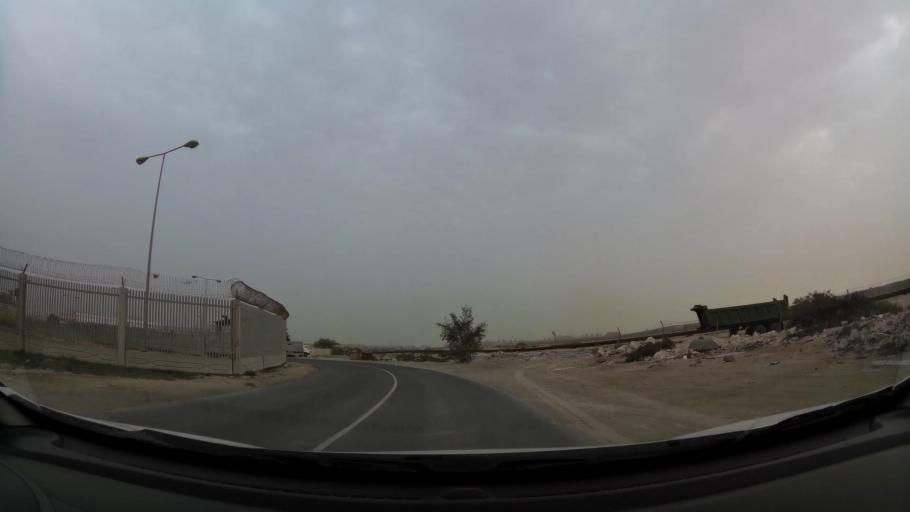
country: BH
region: Northern
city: Ar Rifa'
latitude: 26.1179
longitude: 50.5877
